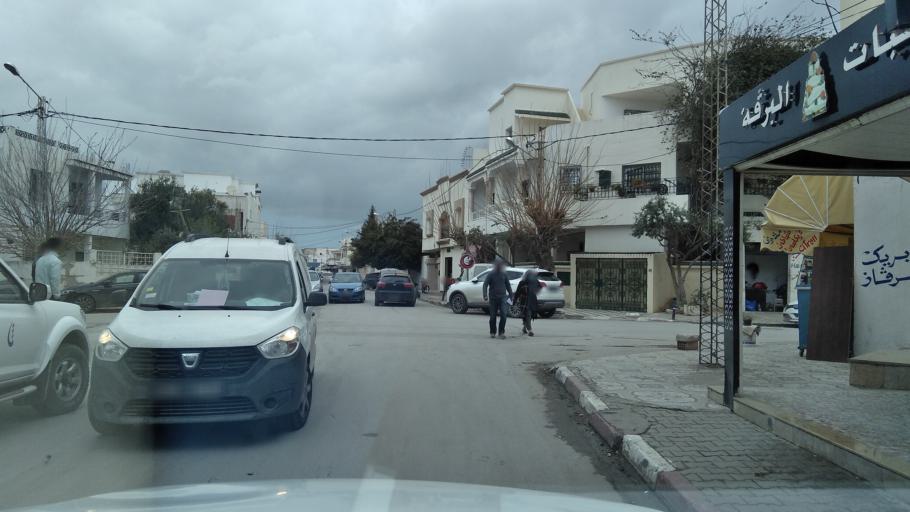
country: TN
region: Bin 'Arus
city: Ben Arous
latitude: 36.7596
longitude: 10.2260
